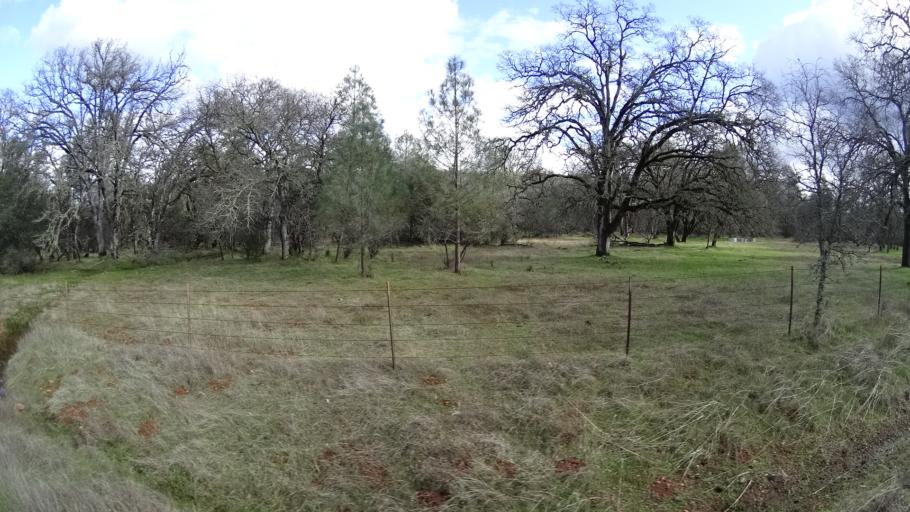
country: US
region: California
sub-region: Butte County
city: Oroville
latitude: 39.6225
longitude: -121.5281
